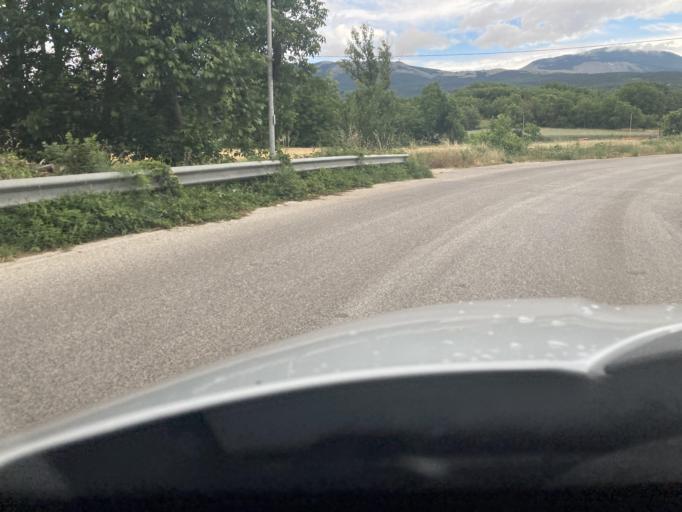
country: IT
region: Abruzzo
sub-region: Provincia dell' Aquila
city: Sant'Eusanio Forconese
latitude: 42.2933
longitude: 13.5292
